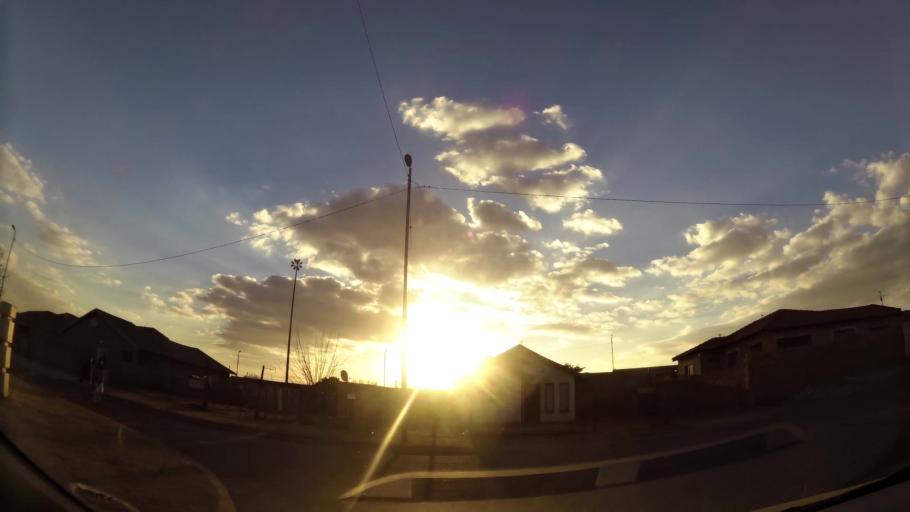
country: ZA
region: Gauteng
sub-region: West Rand District Municipality
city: Krugersdorp
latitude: -26.0763
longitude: 27.7547
